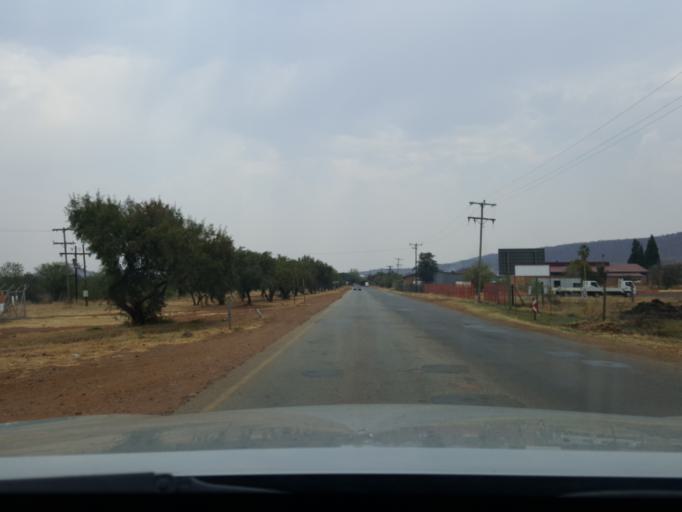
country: ZA
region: North-West
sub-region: Ngaka Modiri Molema District Municipality
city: Zeerust
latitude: -25.5031
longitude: 25.9837
